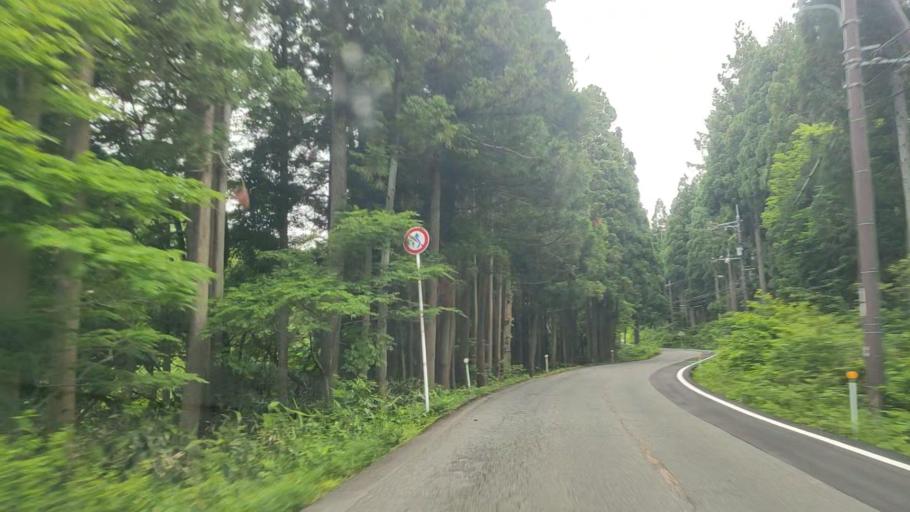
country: JP
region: Tottori
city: Yonago
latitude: 35.3337
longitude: 133.5570
